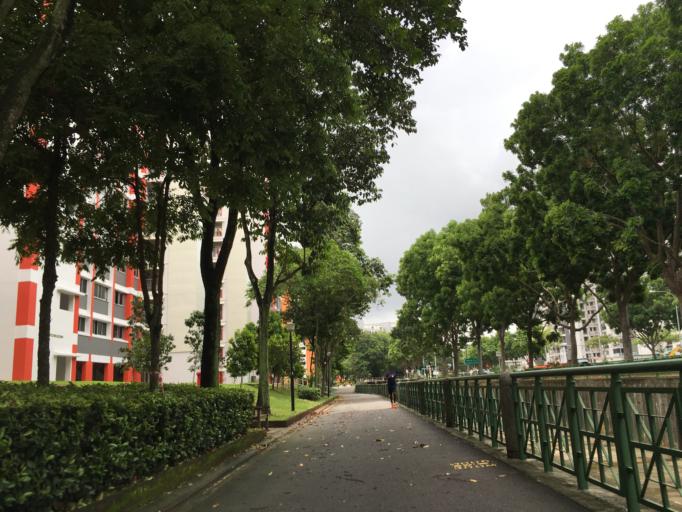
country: MY
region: Johor
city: Kampung Pasir Gudang Baru
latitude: 1.3797
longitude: 103.8942
